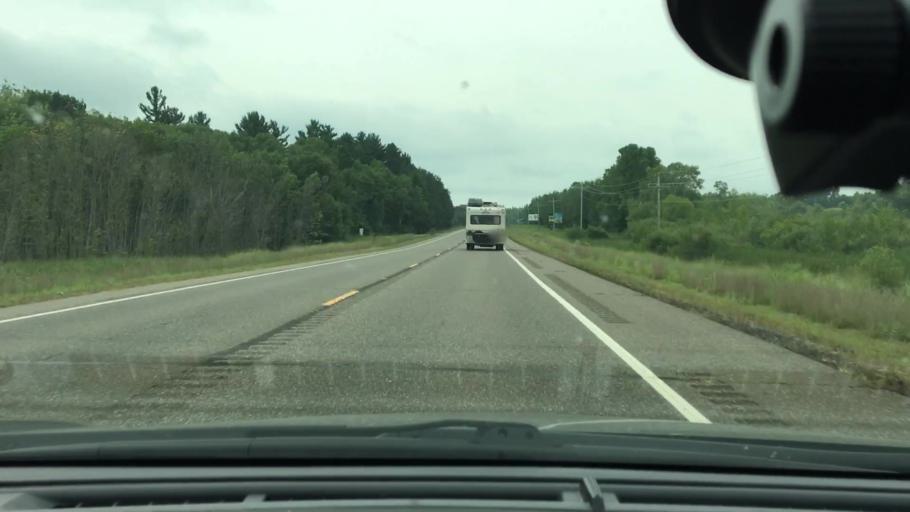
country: US
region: Minnesota
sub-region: Crow Wing County
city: Crosby
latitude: 46.5026
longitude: -93.9571
